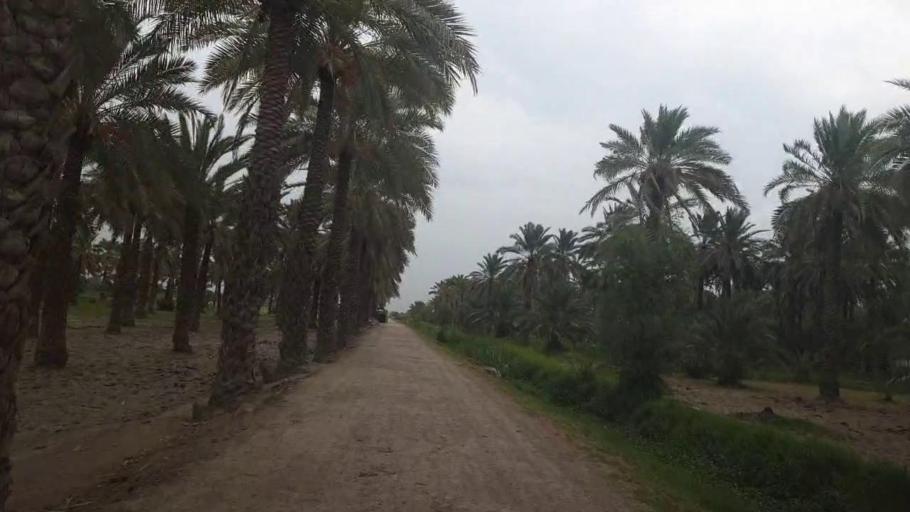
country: PK
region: Sindh
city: Khairpur
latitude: 27.5611
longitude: 68.7107
